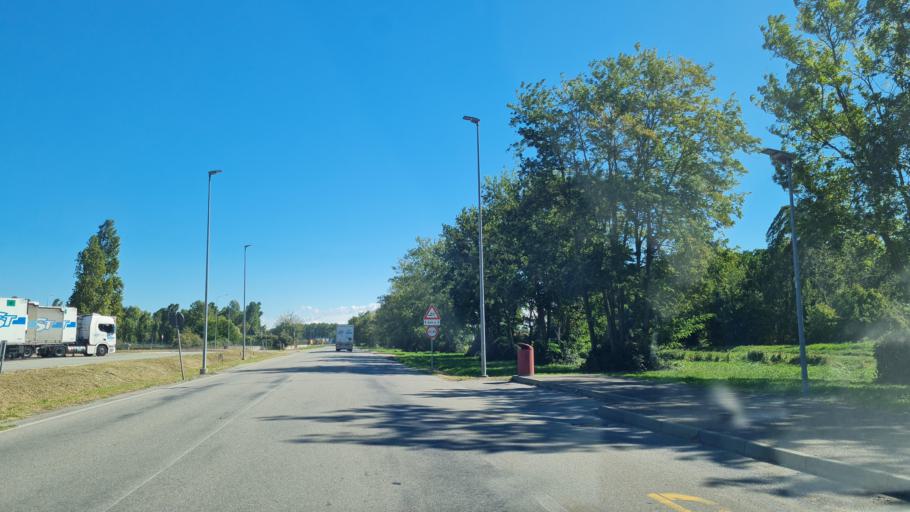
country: IT
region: Piedmont
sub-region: Provincia di Novara
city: Biandrate
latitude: 45.4582
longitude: 8.4583
